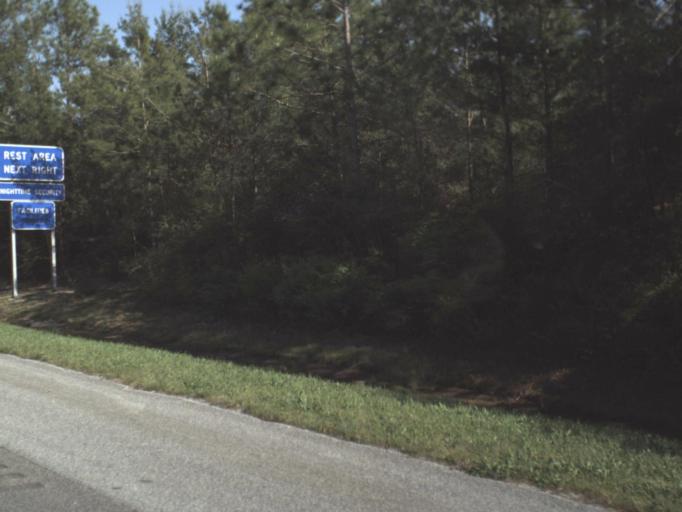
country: US
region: Florida
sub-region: Okaloosa County
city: Crestview
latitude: 30.7268
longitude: -86.5132
